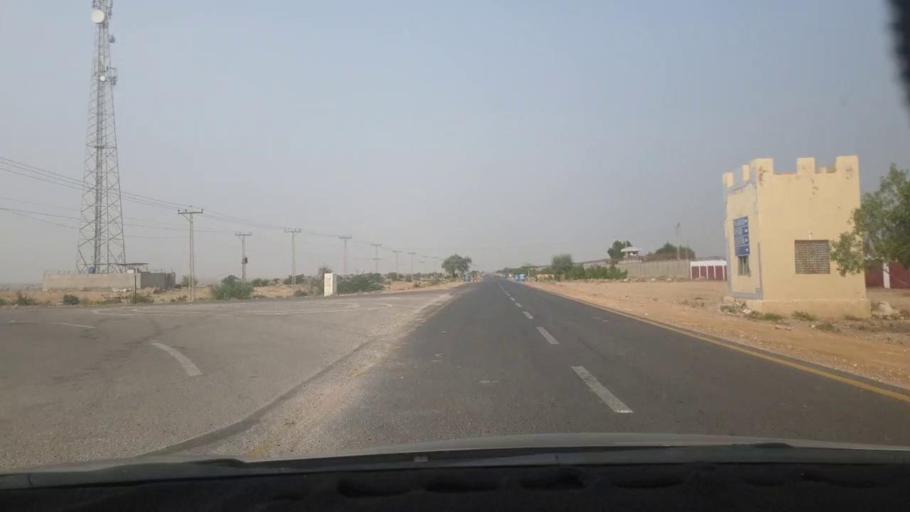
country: PK
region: Sindh
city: Jamshoro
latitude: 25.5436
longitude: 68.3206
